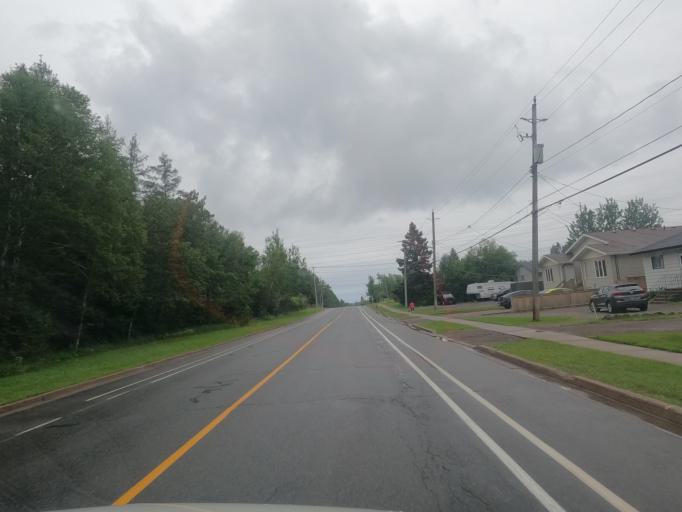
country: CA
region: Ontario
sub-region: Thunder Bay District
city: Thunder Bay
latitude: 48.4760
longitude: -89.1822
